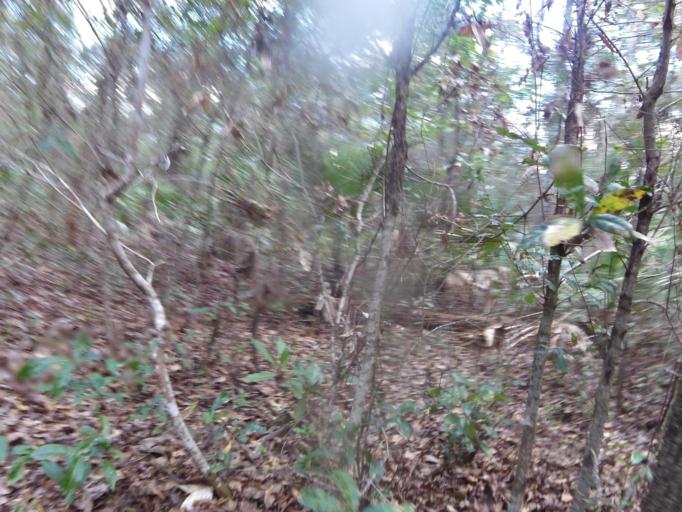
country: US
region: Florida
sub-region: Putnam County
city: Interlachen
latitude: 29.7631
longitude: -81.8276
